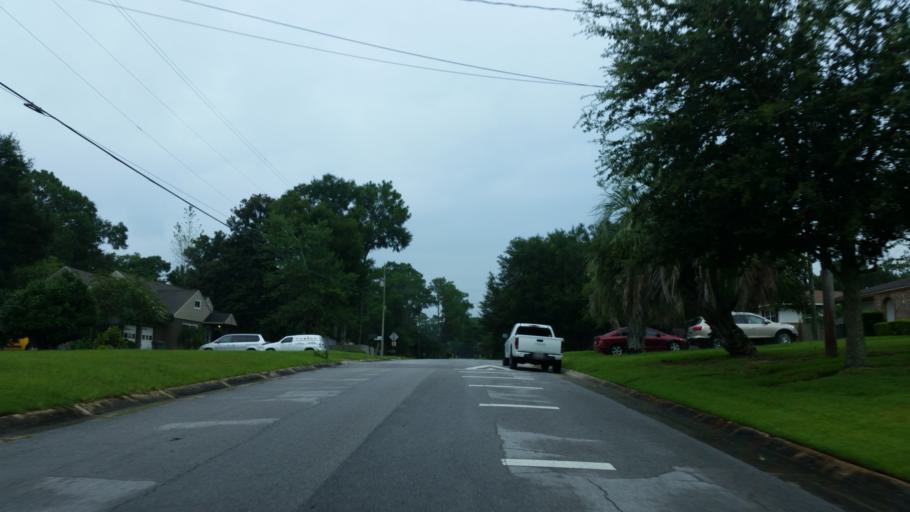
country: US
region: Florida
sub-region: Escambia County
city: Brent
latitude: 30.4920
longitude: -87.2393
